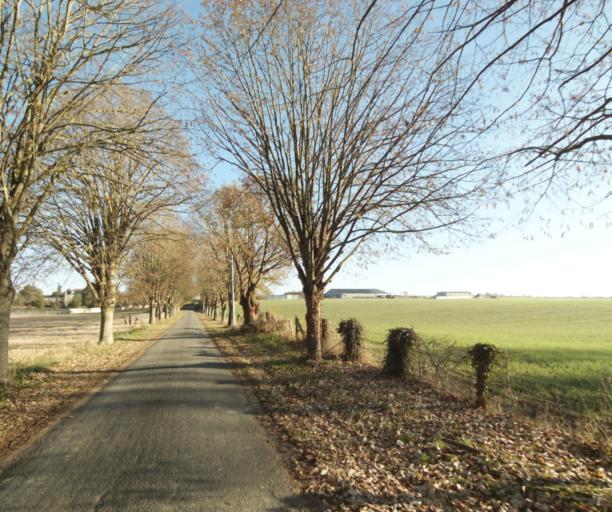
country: FR
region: Poitou-Charentes
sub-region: Departement de la Charente-Maritime
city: Cherac
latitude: 45.6893
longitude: -0.4635
